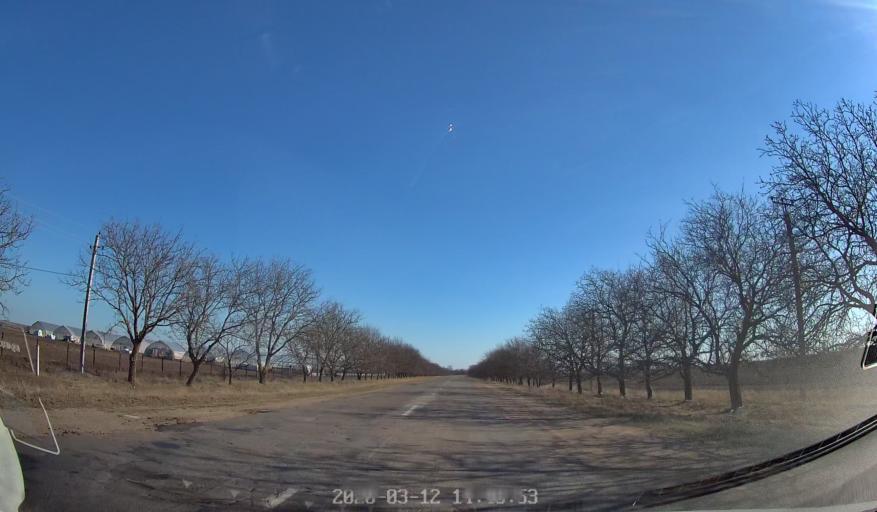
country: MD
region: Criuleni
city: Criuleni
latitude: 47.2287
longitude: 29.1419
